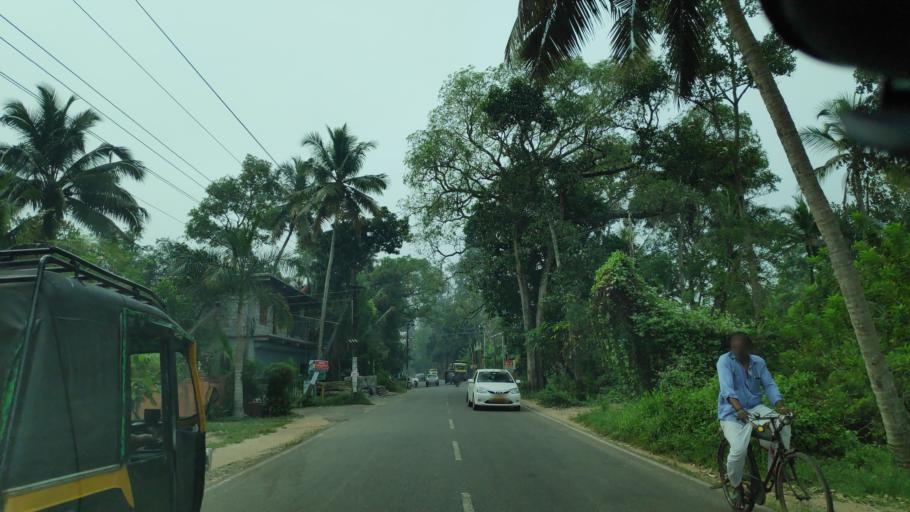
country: IN
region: Kerala
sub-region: Alappuzha
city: Alleppey
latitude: 9.5844
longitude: 76.3513
